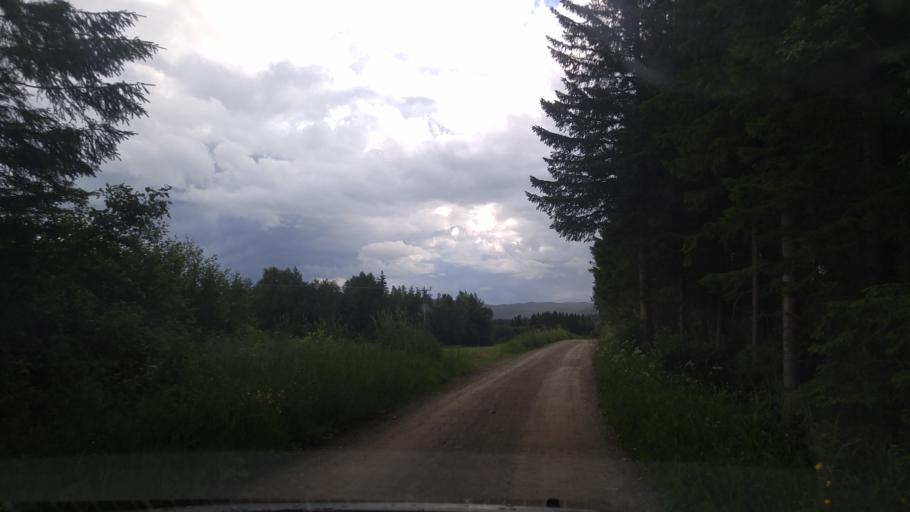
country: NO
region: Nord-Trondelag
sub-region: Levanger
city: Skogn
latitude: 63.6290
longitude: 11.2661
